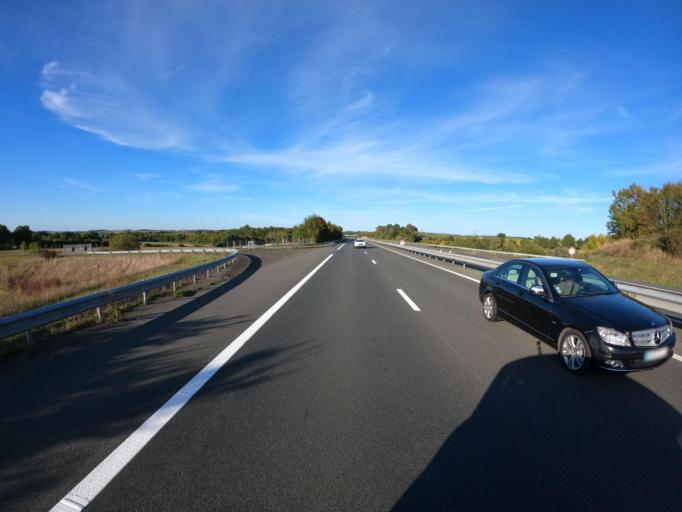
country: FR
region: Pays de la Loire
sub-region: Departement de Maine-et-Loire
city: Saint-Lambert-du-Lattay
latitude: 47.2931
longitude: -0.6129
